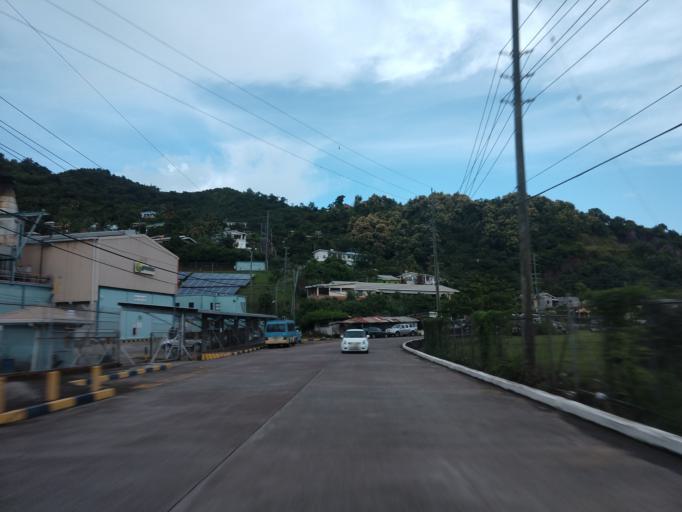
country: GD
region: Saint George
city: Saint George's
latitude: 12.0616
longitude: -61.7528
